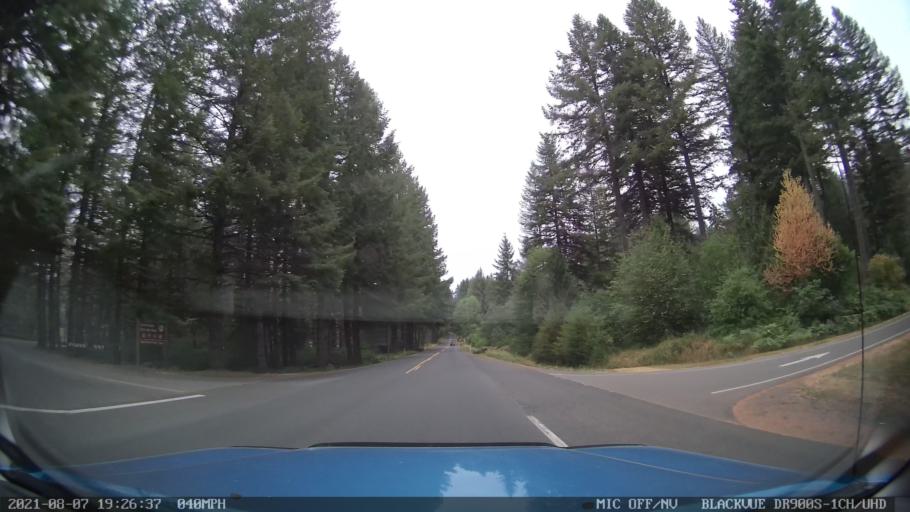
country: US
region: Oregon
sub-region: Linn County
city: Lyons
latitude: 44.8736
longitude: -122.6516
